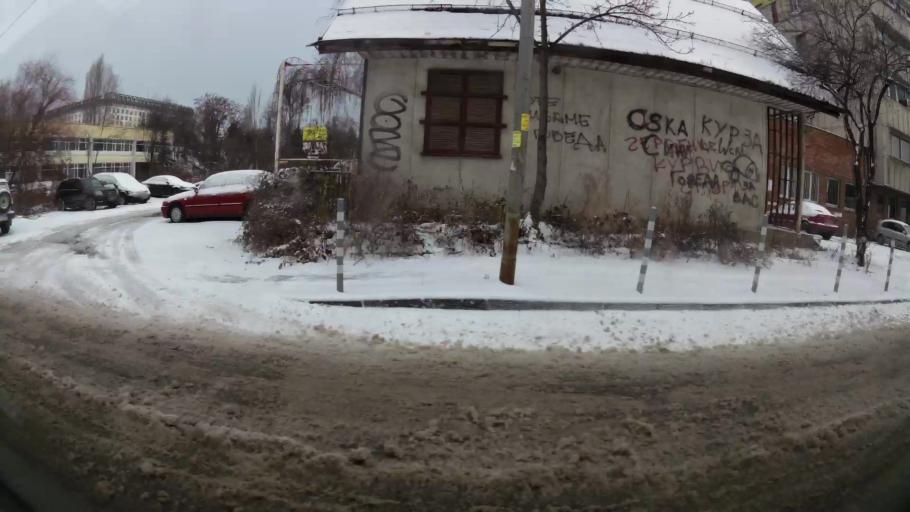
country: BG
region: Sofia-Capital
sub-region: Stolichna Obshtina
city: Sofia
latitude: 42.6930
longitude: 23.3050
